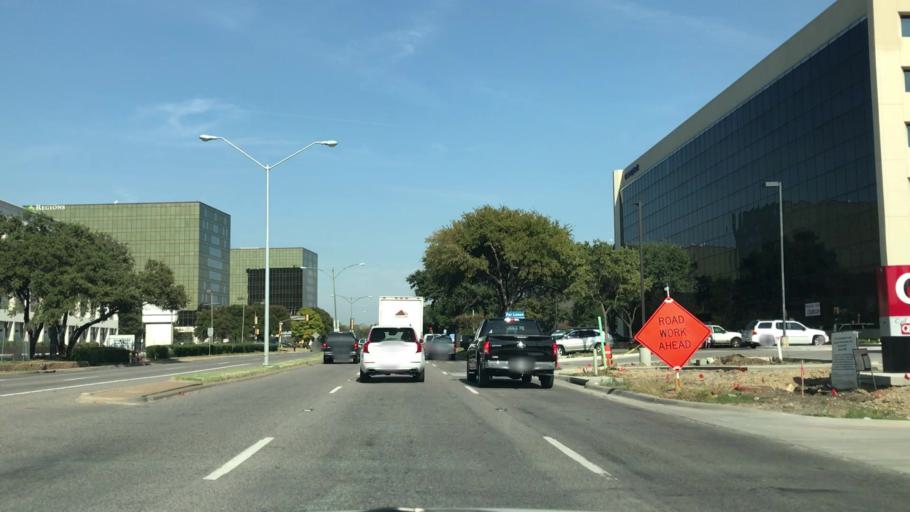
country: US
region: Texas
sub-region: Dallas County
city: Dallas
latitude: 32.8196
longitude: -96.8681
